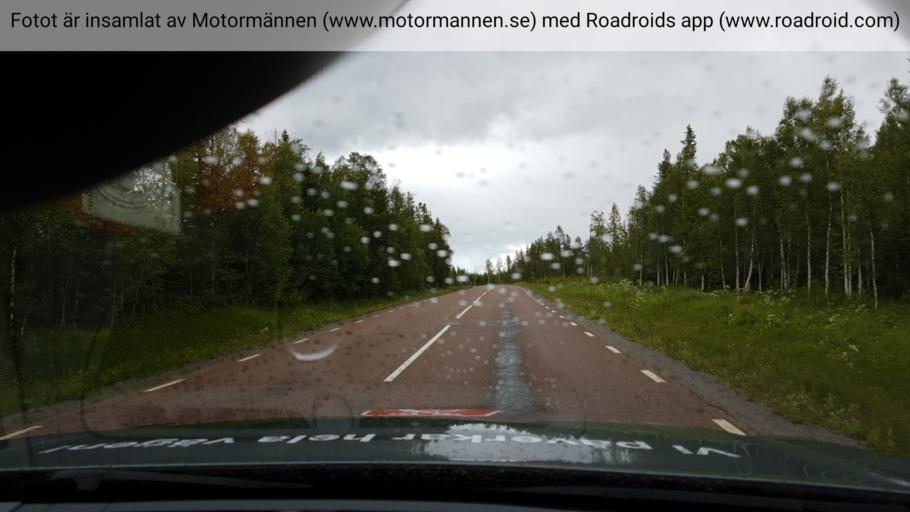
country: SE
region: Jaemtland
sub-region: Krokoms Kommun
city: Valla
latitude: 63.1223
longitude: 13.9246
